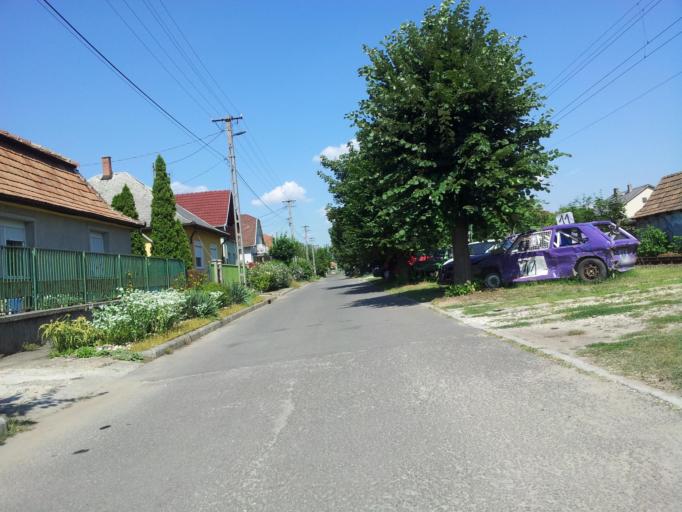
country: HU
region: Pest
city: Veresegyhaz
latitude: 47.6459
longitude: 19.2838
